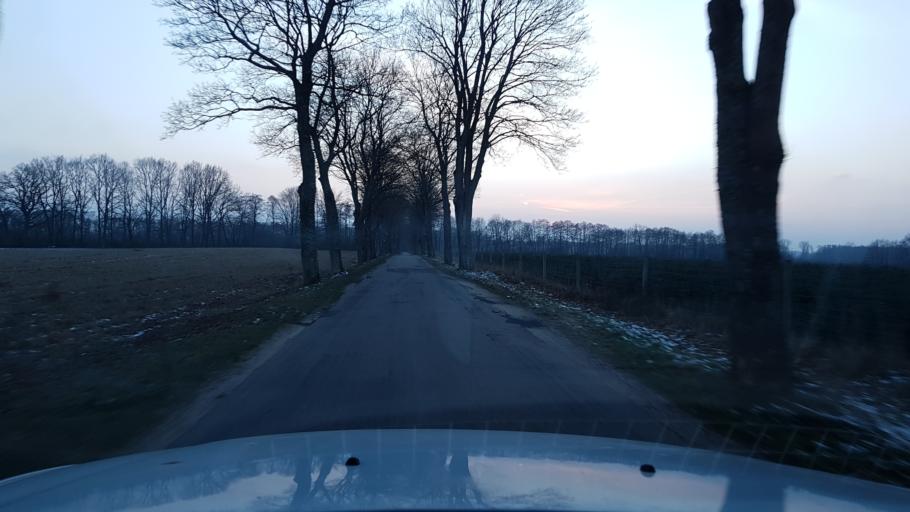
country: PL
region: West Pomeranian Voivodeship
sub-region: Powiat bialogardzki
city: Karlino
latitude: 54.0081
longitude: 15.8377
